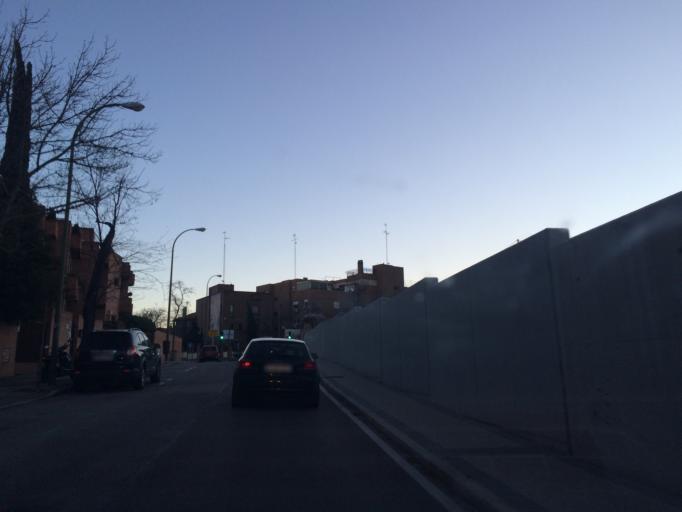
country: ES
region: Madrid
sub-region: Provincia de Madrid
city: Chamartin
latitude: 40.4681
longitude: -3.6827
